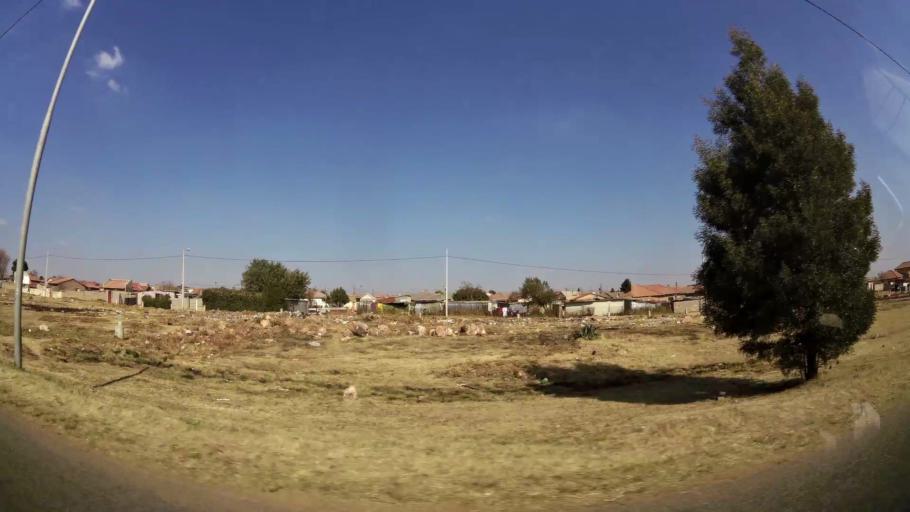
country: ZA
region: Gauteng
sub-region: City of Johannesburg Metropolitan Municipality
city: Roodepoort
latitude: -26.1716
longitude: 27.7879
